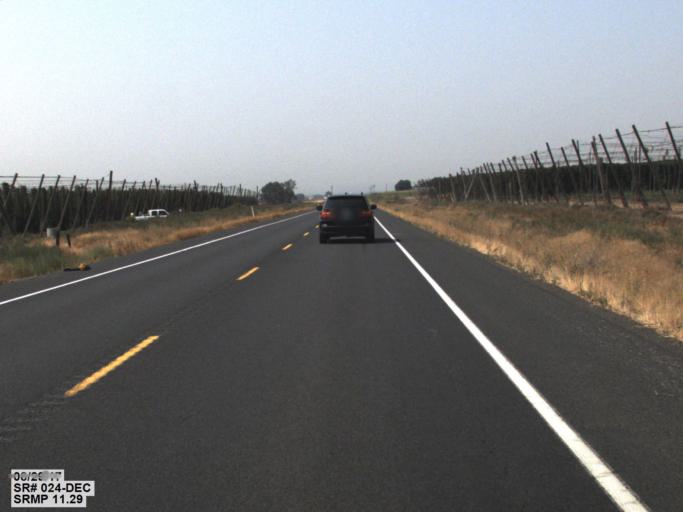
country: US
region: Washington
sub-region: Yakima County
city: Zillah
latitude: 46.5277
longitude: -120.2625
